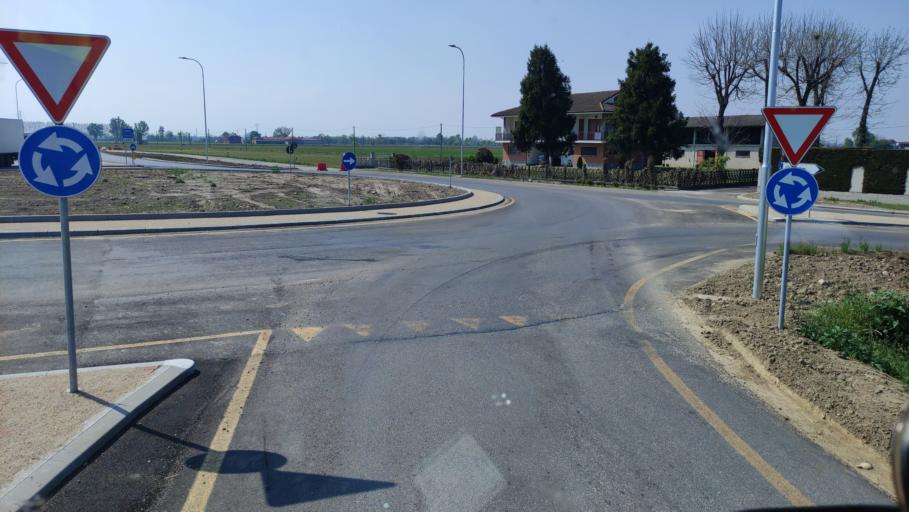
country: IT
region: Piedmont
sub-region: Provincia di Cuneo
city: Marene
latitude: 44.6566
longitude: 7.7164
